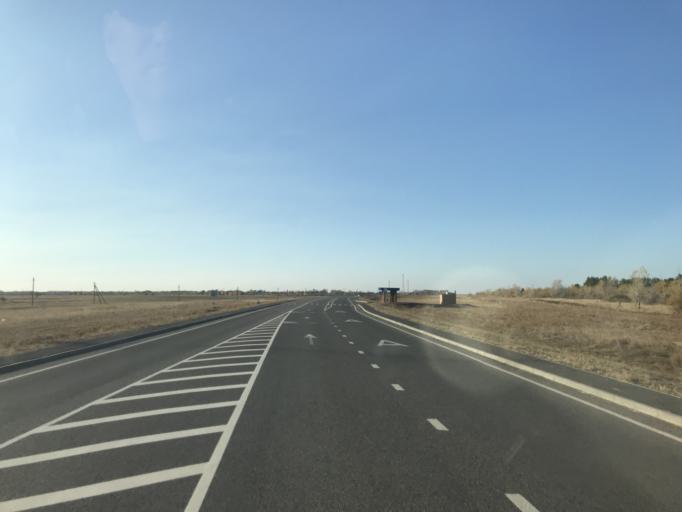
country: KZ
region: Pavlodar
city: Koktobe
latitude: 51.9098
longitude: 77.3570
